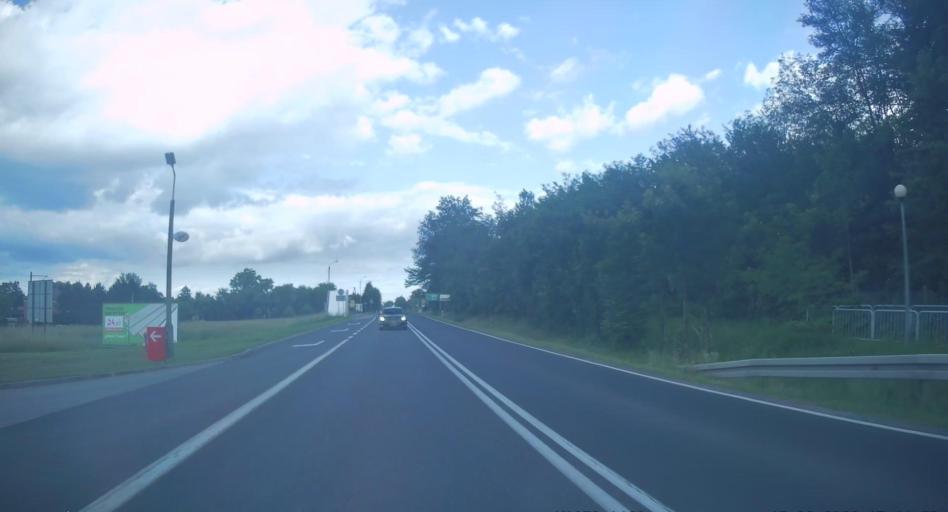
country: PL
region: Lesser Poland Voivodeship
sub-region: Powiat oswiecimski
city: Bulowice
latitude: 49.8798
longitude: 19.2599
